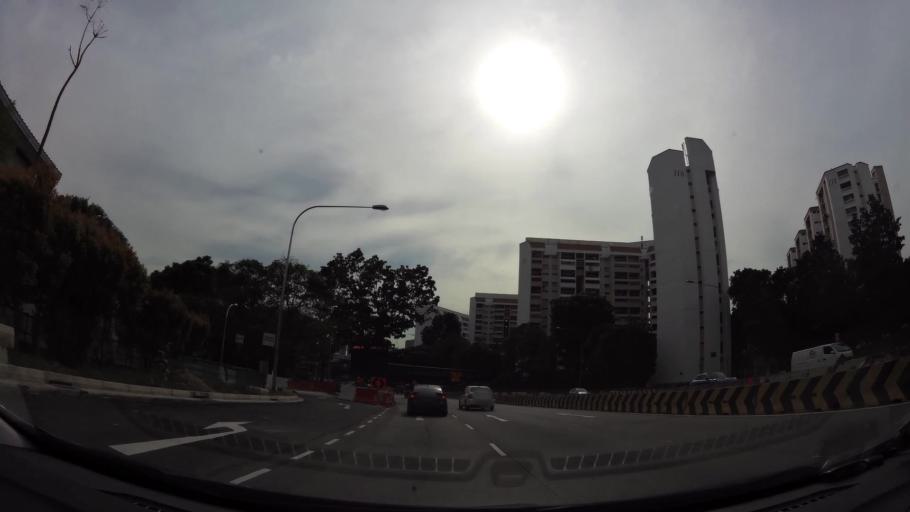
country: SG
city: Singapore
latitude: 1.3244
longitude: 103.7730
